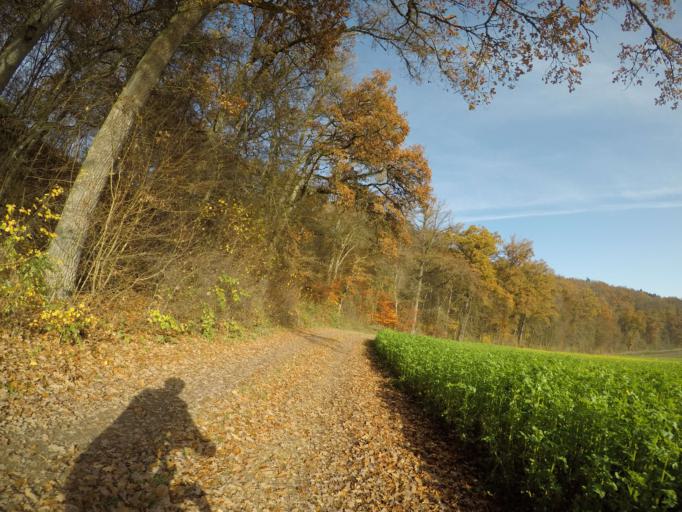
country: DE
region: Baden-Wuerttemberg
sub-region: Tuebingen Region
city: Bernstadt
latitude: 48.5147
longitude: 10.0172
